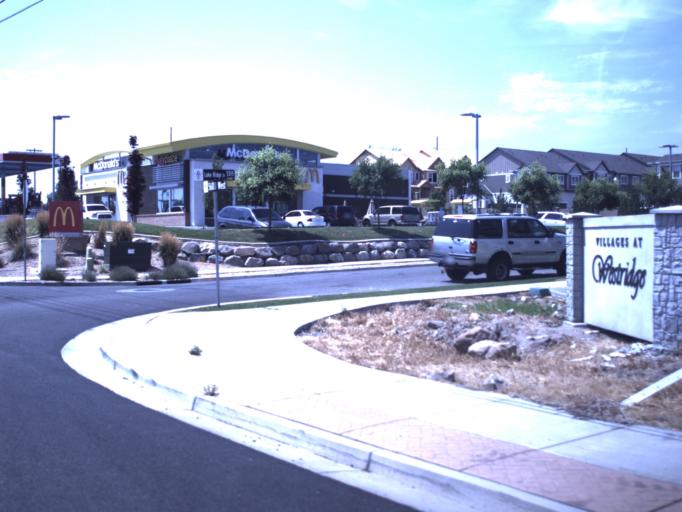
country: US
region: Utah
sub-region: Salt Lake County
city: Oquirrh
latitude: 40.6547
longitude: -112.0248
